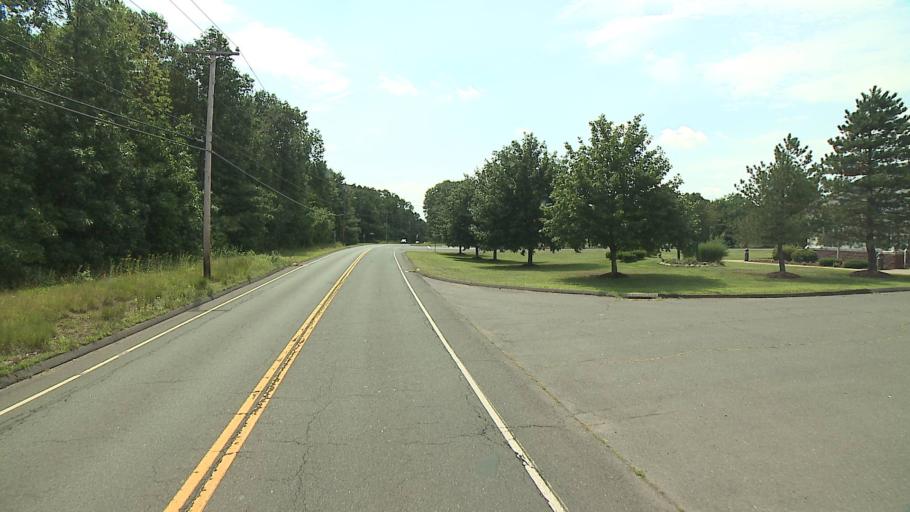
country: US
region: Connecticut
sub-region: Hartford County
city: Plainville
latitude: 41.7108
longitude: -72.8807
